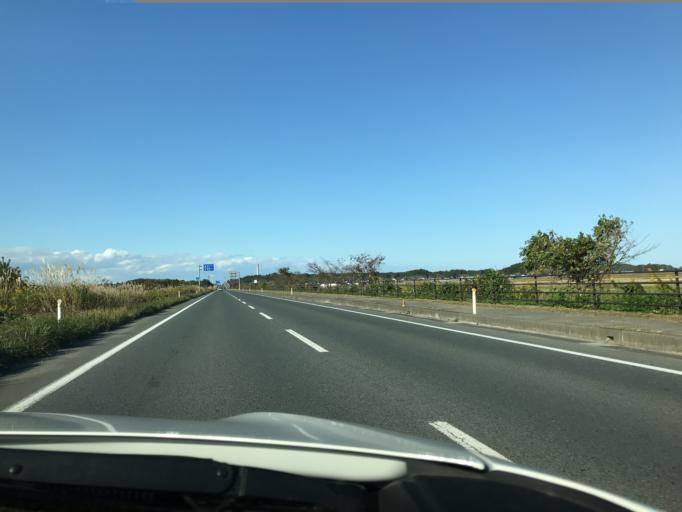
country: JP
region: Miyagi
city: Marumori
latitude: 37.7945
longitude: 140.9438
